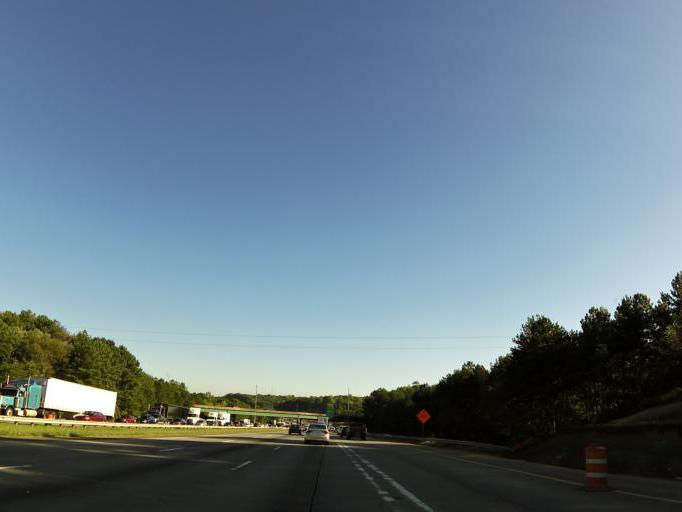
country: US
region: Georgia
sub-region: Cobb County
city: Marietta
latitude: 34.0025
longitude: -84.5637
